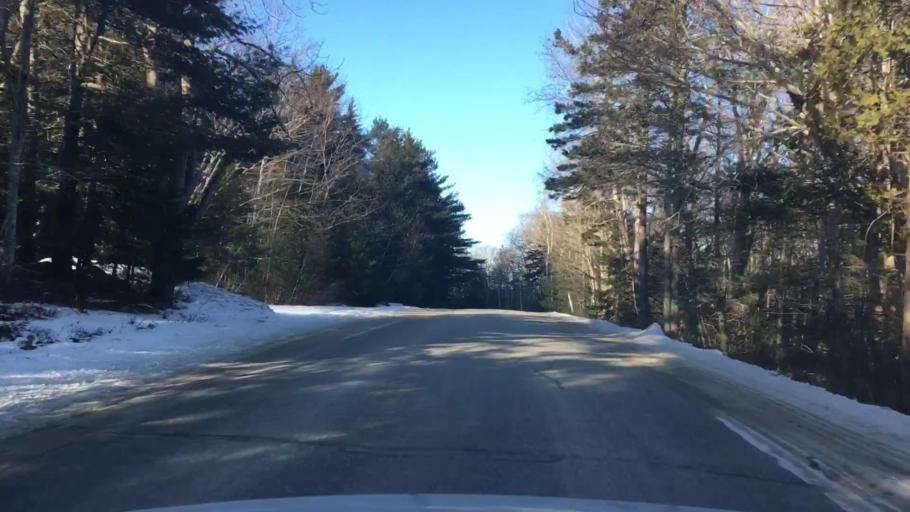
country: US
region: Maine
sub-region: Hancock County
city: Castine
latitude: 44.3528
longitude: -68.7792
